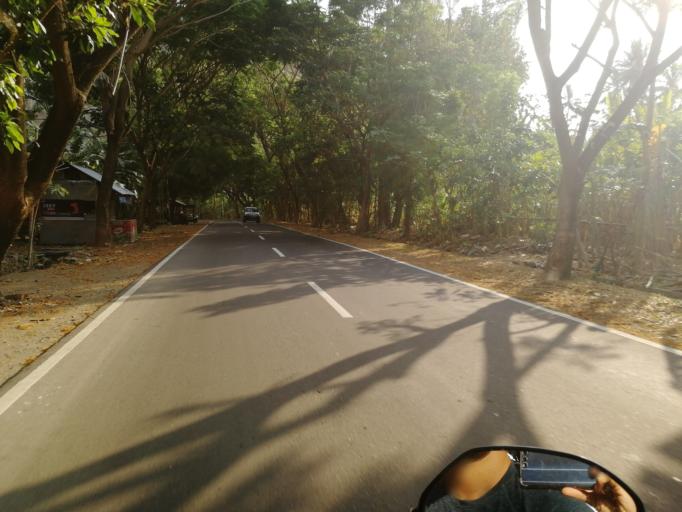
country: ID
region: West Nusa Tenggara
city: Karangsubagan
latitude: -8.4427
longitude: 116.0419
